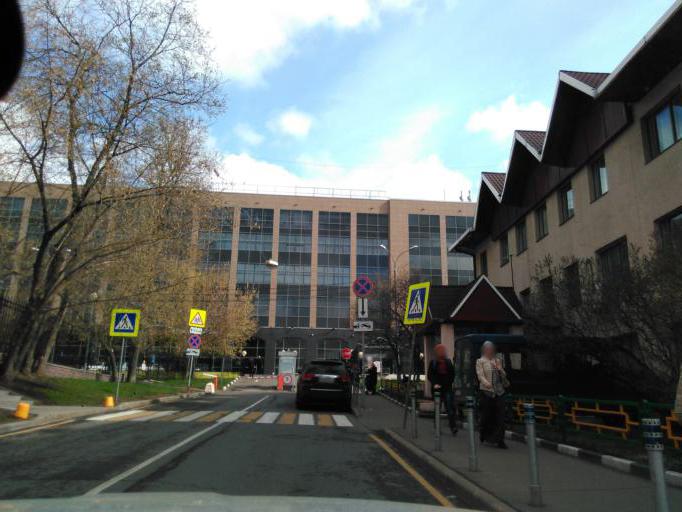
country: RU
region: Moskovskaya
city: Dorogomilovo
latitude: 55.7573
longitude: 37.5719
